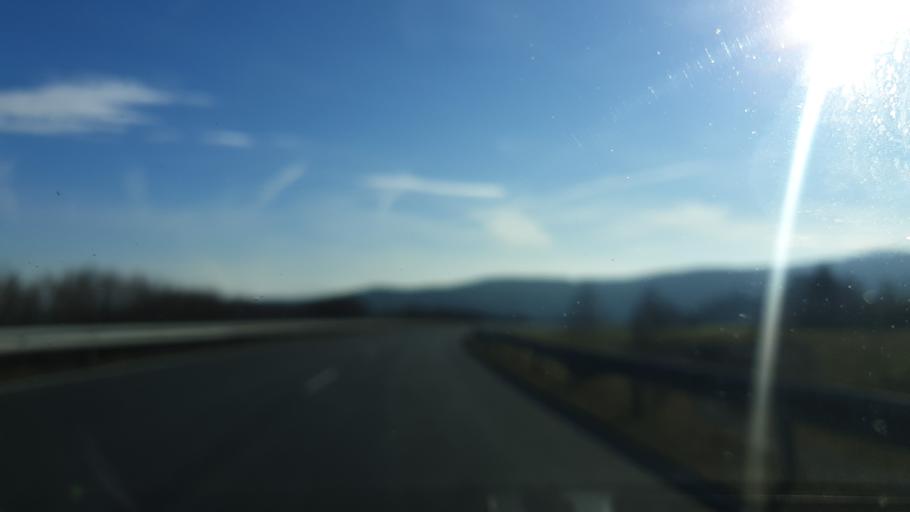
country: DE
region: Saxony
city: Bad Brambach
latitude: 50.2293
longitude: 12.3187
